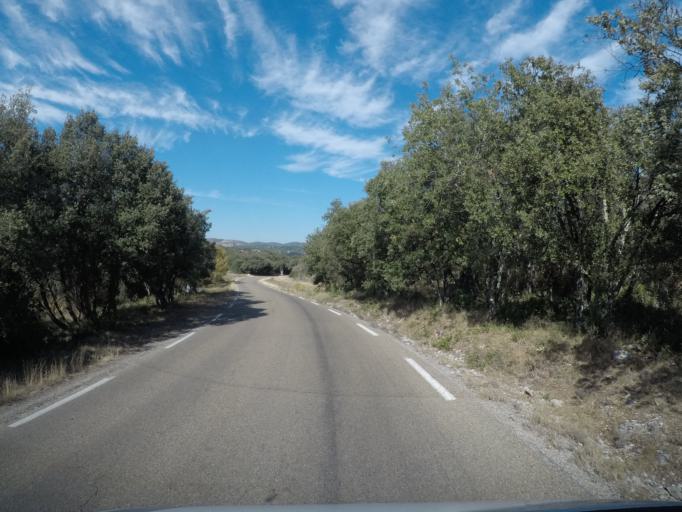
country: FR
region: Languedoc-Roussillon
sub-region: Departement du Gard
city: Boisset-et-Gaujac
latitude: 44.0127
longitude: 3.9936
